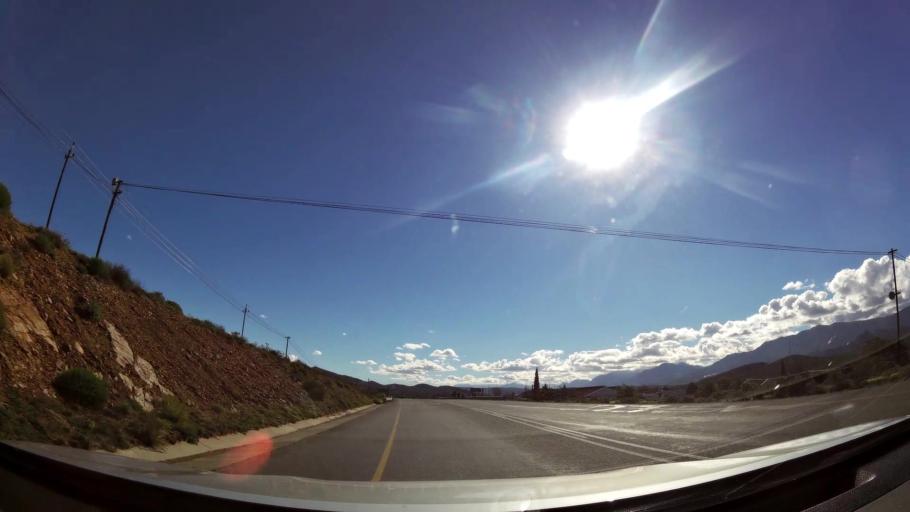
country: ZA
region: Western Cape
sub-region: Cape Winelands District Municipality
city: Ashton
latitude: -33.7780
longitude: 19.7632
